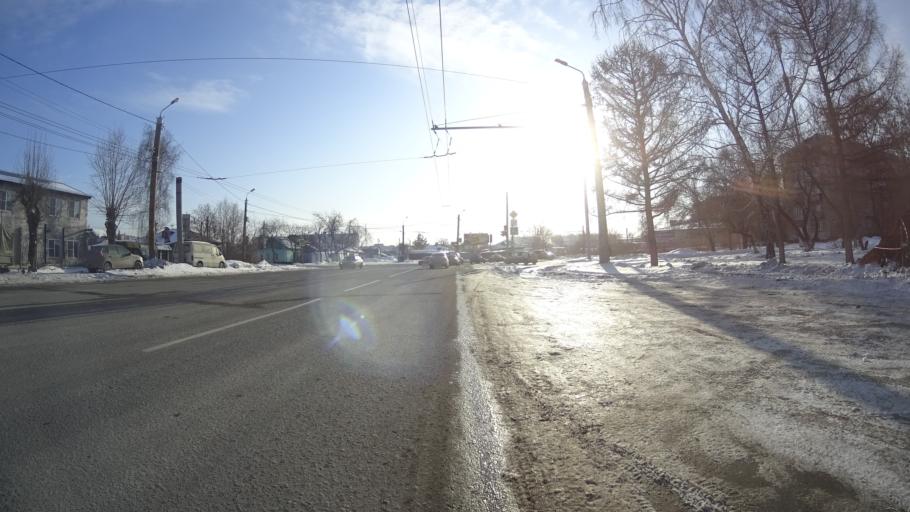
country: RU
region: Chelyabinsk
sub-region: Gorod Chelyabinsk
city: Chelyabinsk
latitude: 55.1844
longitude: 61.4588
